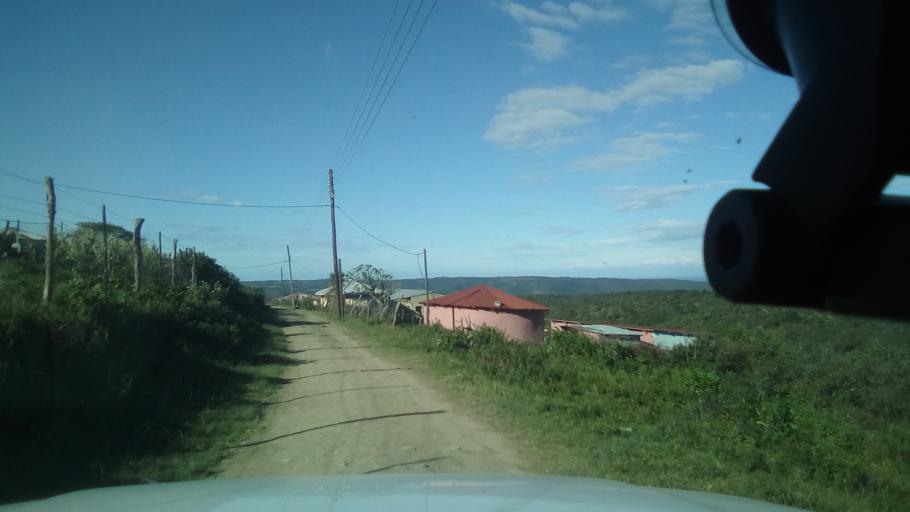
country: ZA
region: Eastern Cape
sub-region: Amathole District Municipality
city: Komga
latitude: -32.7729
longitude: 27.9450
